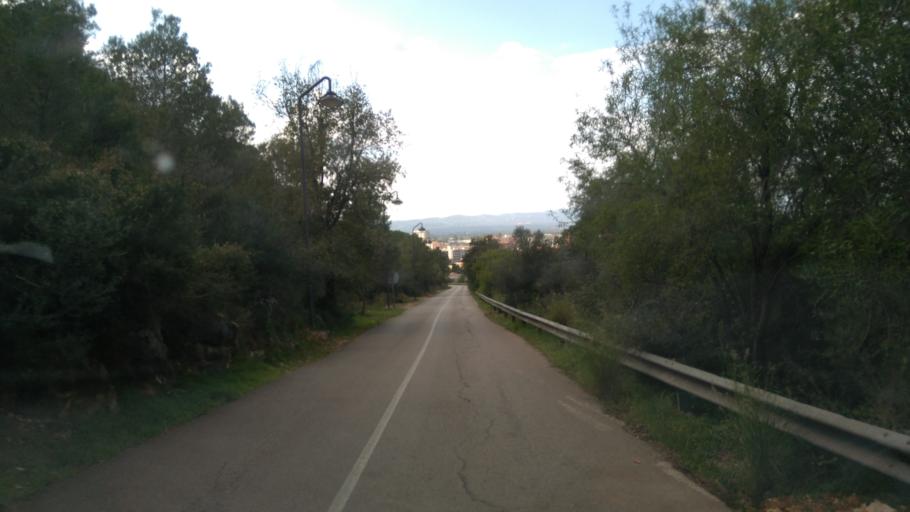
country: ES
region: Valencia
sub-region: Provincia de Valencia
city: Alzira
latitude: 39.1538
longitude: -0.4185
